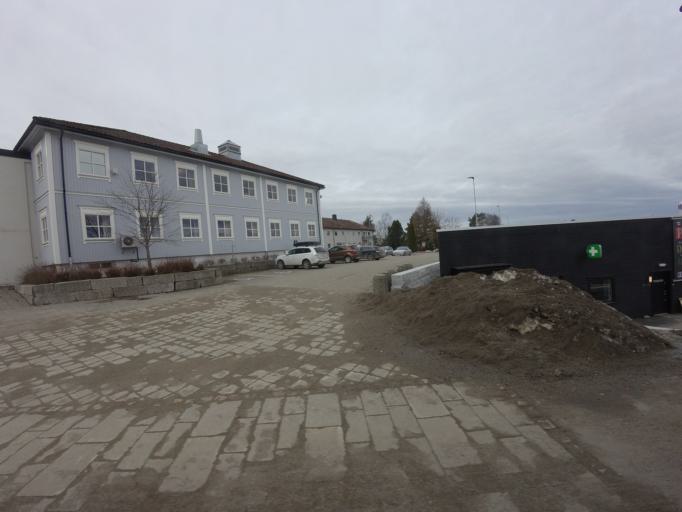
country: NO
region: Ostfold
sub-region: Trogstad
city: Skjonhaug
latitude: 59.6416
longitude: 11.3157
